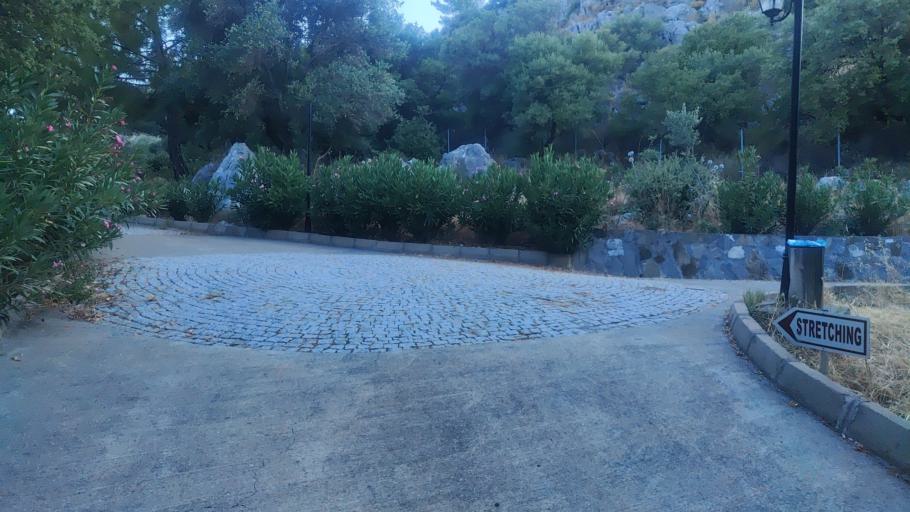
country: TR
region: Mugla
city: Sarigerme
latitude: 36.7053
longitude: 28.6936
